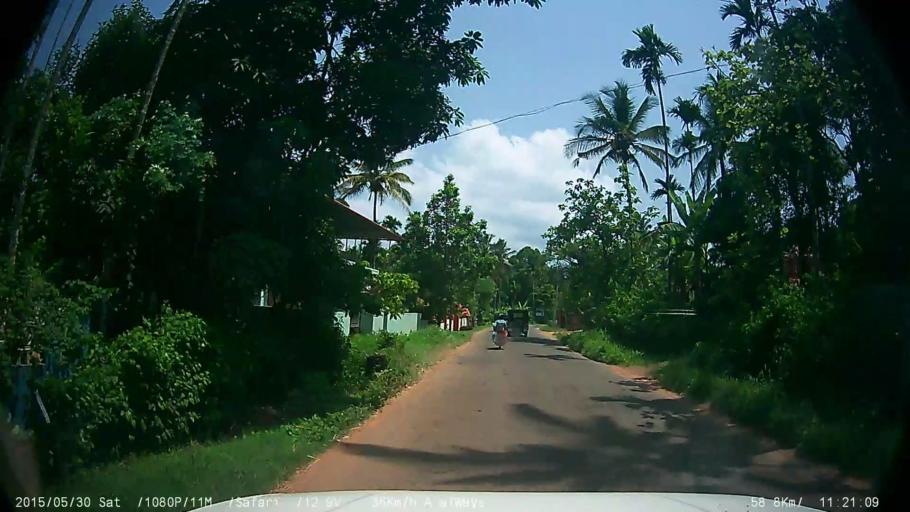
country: IN
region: Kerala
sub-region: Wayanad
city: Panamaram
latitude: 11.7998
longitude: 76.0376
